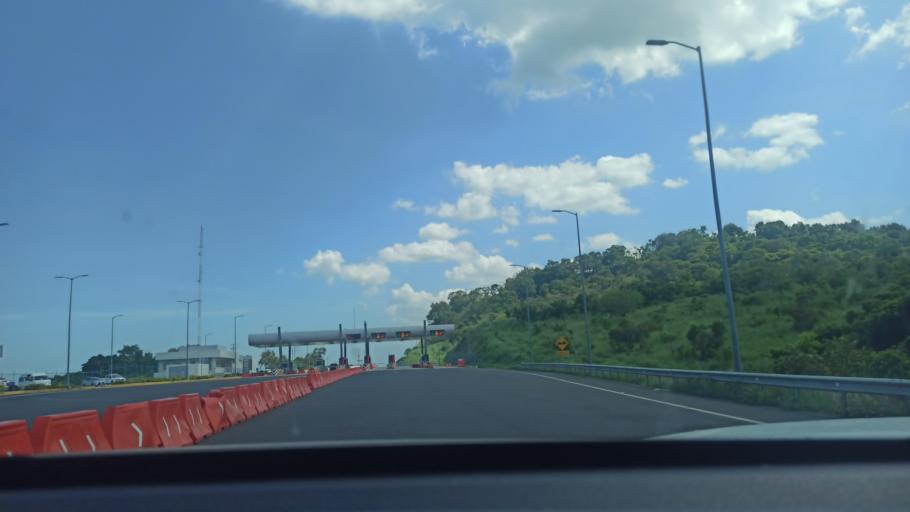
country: MX
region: Veracruz
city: Vega de Alatorre
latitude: 20.0451
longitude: -96.6855
